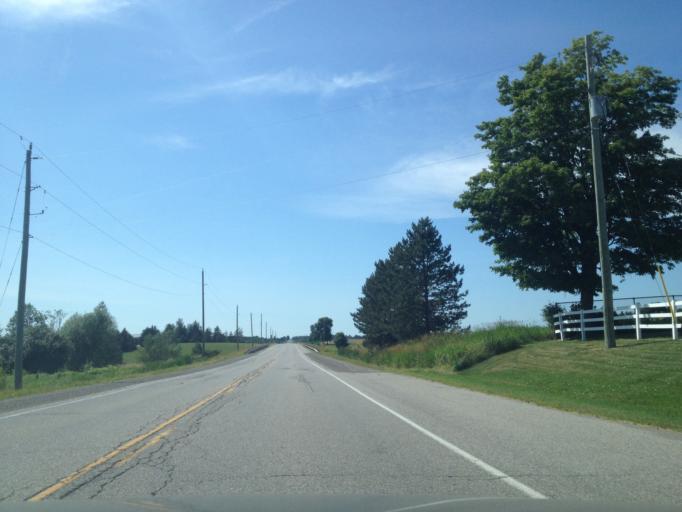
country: CA
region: Ontario
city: Stratford
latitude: 43.4787
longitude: -80.8219
